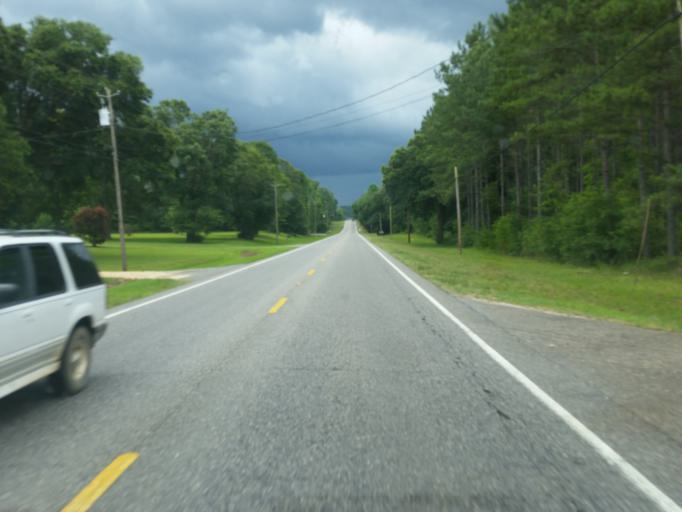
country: US
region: Mississippi
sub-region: Jackson County
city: Hurley
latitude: 30.8145
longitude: -88.3459
